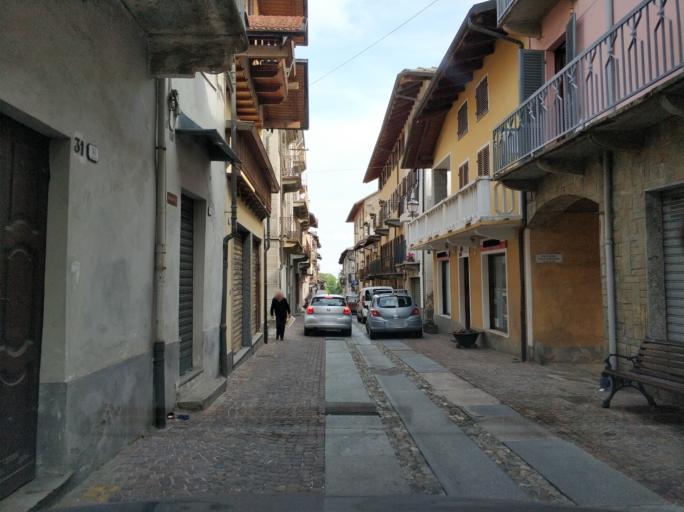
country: IT
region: Piedmont
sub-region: Provincia di Torino
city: Corio
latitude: 45.3126
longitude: 7.5319
